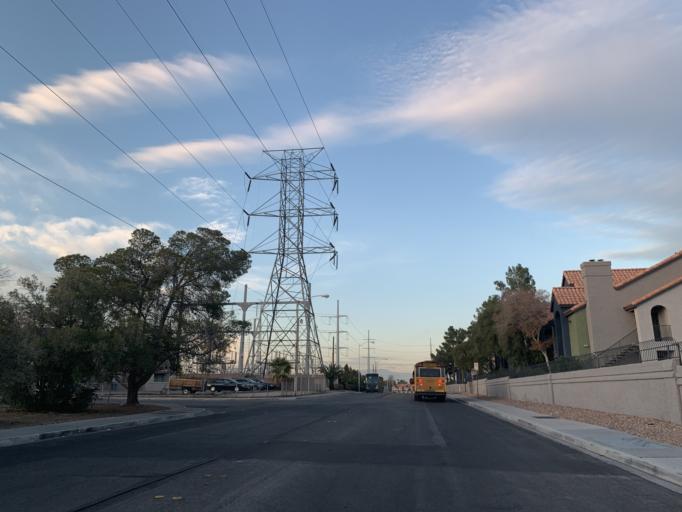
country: US
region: Nevada
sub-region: Clark County
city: Spring Valley
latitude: 36.1124
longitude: -115.2122
